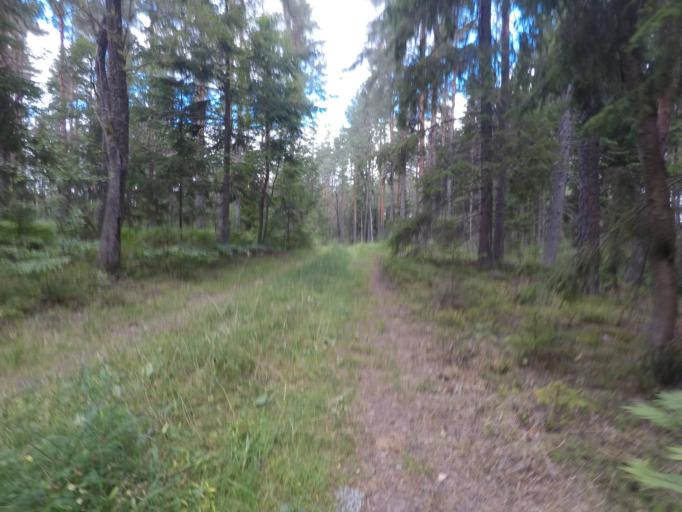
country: SE
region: Soedermanland
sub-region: Eskilstuna Kommun
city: Kvicksund
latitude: 59.4017
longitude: 16.3034
